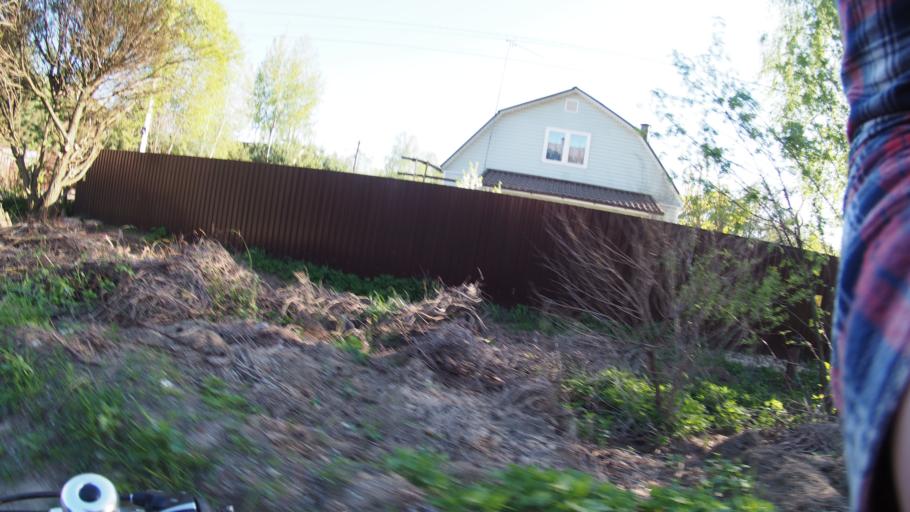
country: RU
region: Moskovskaya
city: Ramenskoye
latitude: 55.5607
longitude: 38.2042
